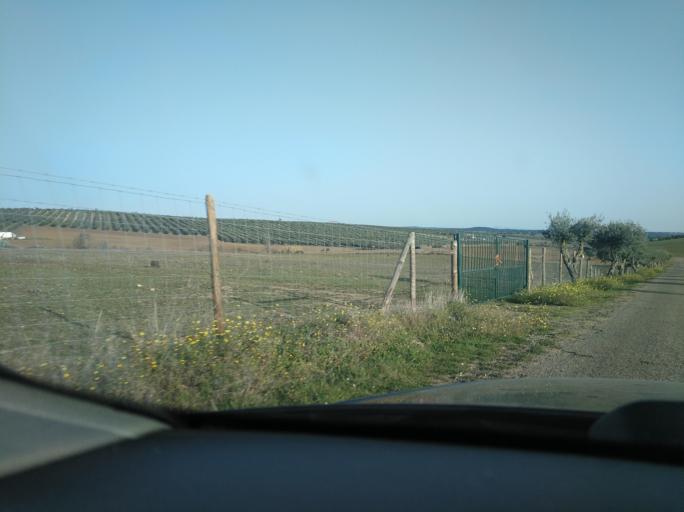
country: PT
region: Portalegre
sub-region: Campo Maior
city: Campo Maior
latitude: 39.0083
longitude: -7.0242
